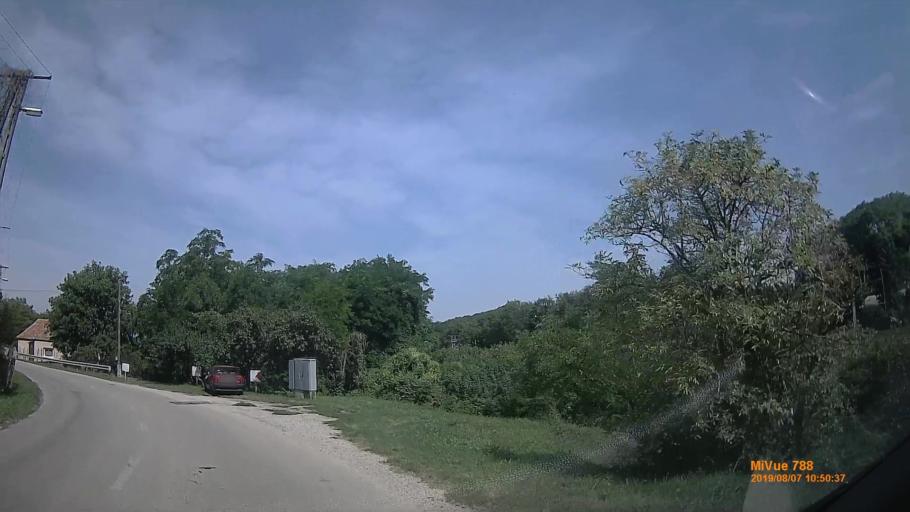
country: HU
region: Veszprem
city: Ajka
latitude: 47.0847
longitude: 17.5717
